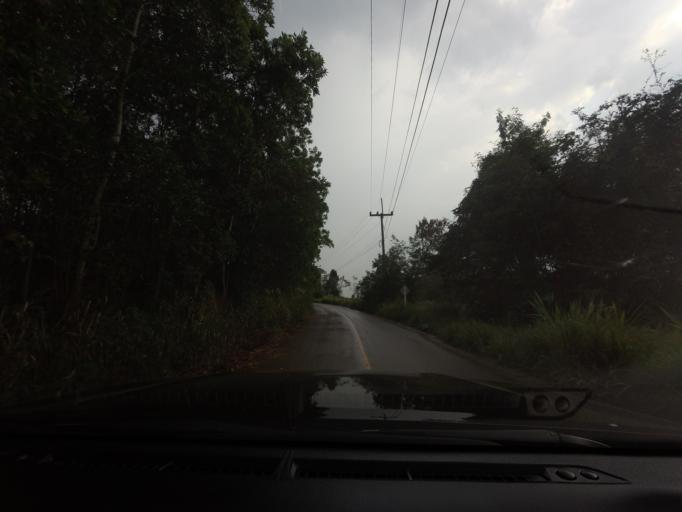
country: TH
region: Nakhon Ratchasima
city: Wang Nam Khiao
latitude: 14.4344
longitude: 101.7102
